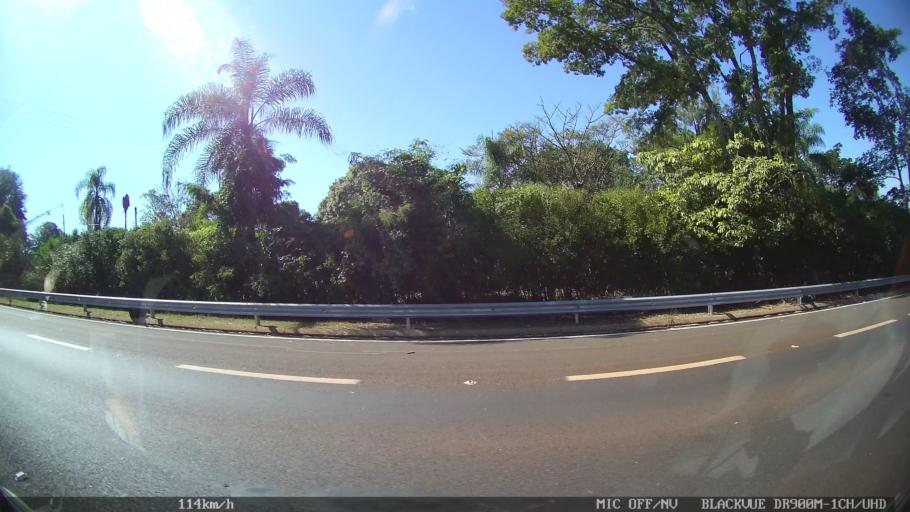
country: BR
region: Sao Paulo
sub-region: Batatais
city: Batatais
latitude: -20.8509
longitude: -47.6010
